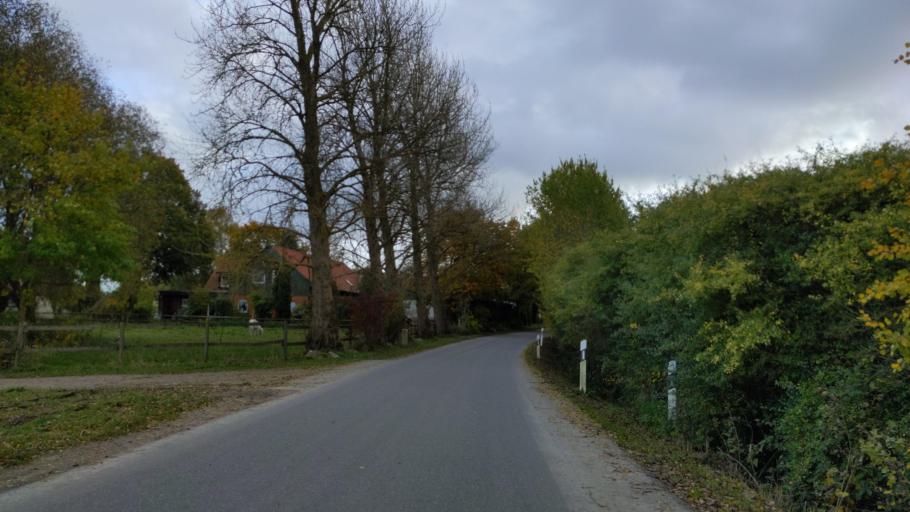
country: DE
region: Schleswig-Holstein
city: Kasseedorf
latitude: 54.1300
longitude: 10.7045
